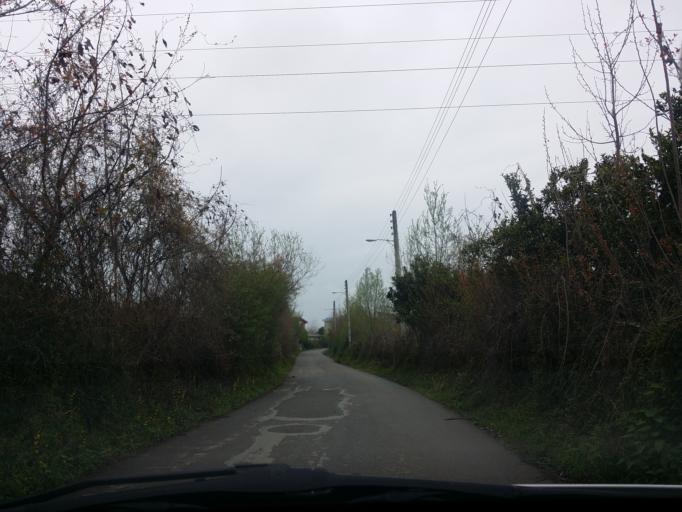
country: IR
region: Mazandaran
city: Chalus
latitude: 36.6742
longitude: 51.3790
